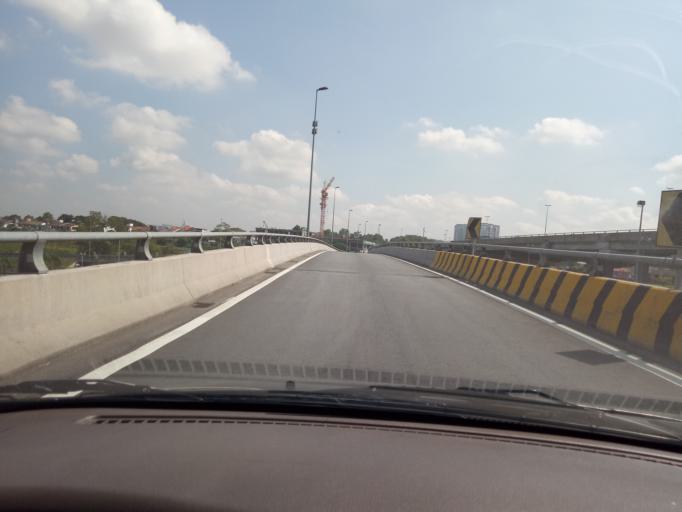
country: MY
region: Selangor
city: Kampong Baharu Balakong
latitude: 3.0619
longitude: 101.6835
